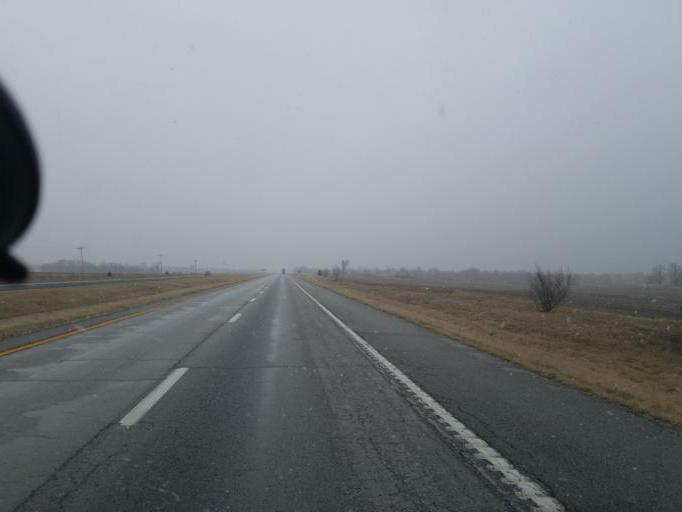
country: US
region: Missouri
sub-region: Macon County
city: La Plata
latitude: 39.9367
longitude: -92.4770
